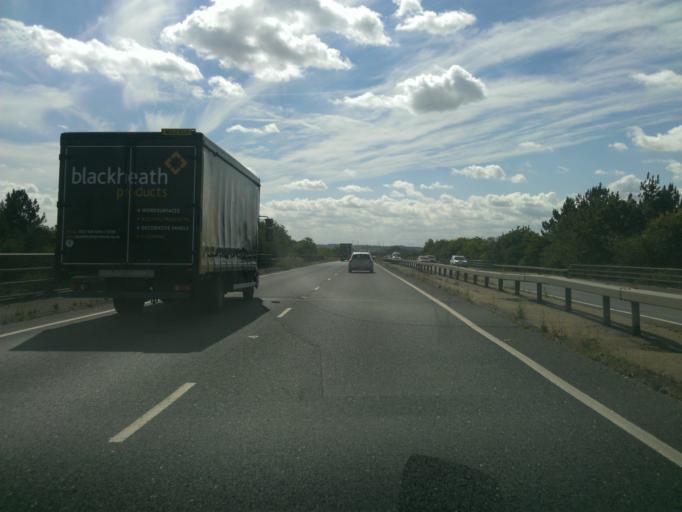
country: GB
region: England
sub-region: Northamptonshire
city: Thrapston
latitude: 52.3919
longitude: -0.5223
